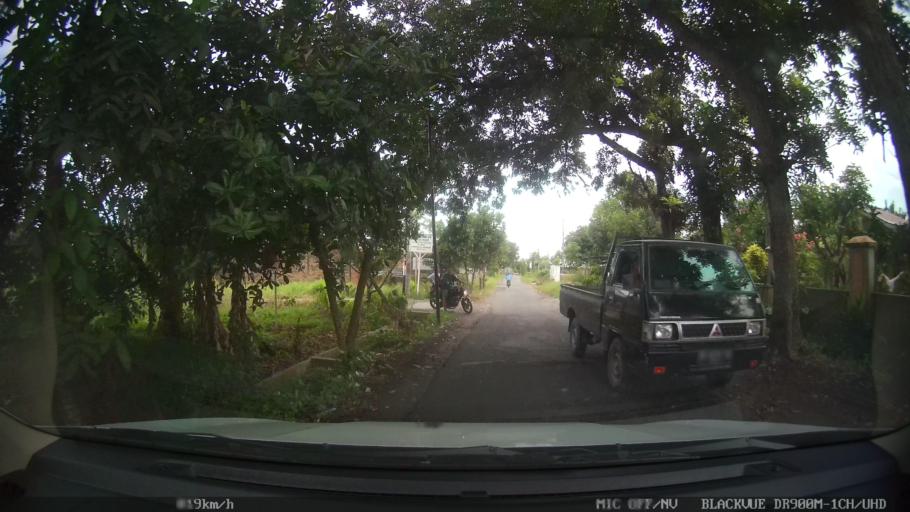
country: ID
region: North Sumatra
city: Sunggal
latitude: 3.5811
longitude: 98.5650
